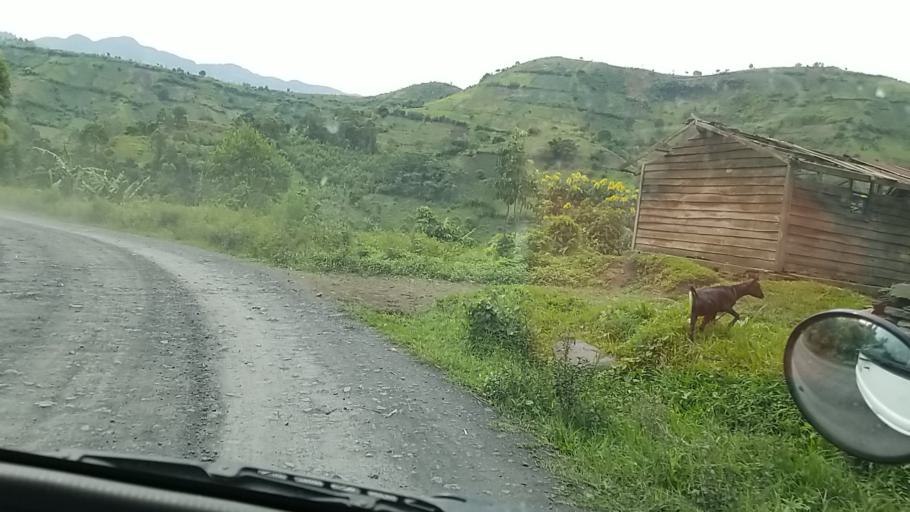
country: CD
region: Nord Kivu
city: Sake
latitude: -1.7377
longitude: 29.0036
